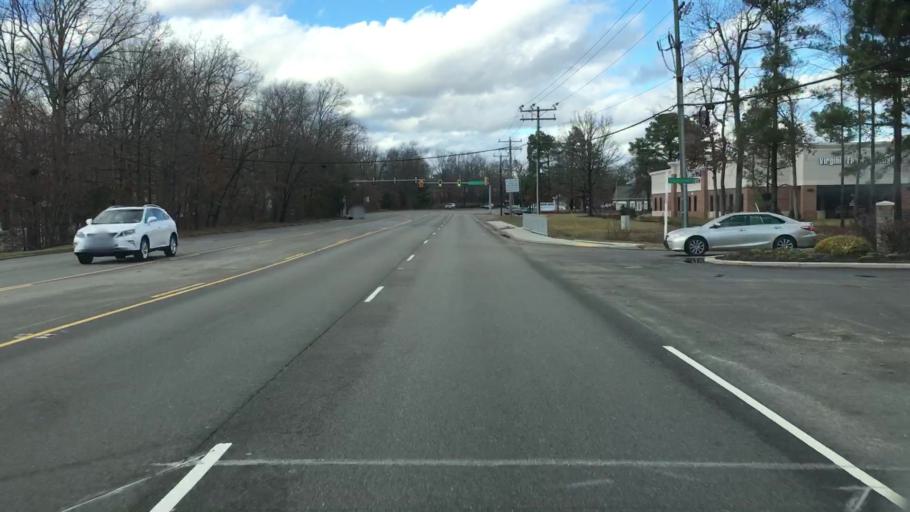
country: US
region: Virginia
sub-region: Chesterfield County
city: Bon Air
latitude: 37.5163
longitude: -77.6155
